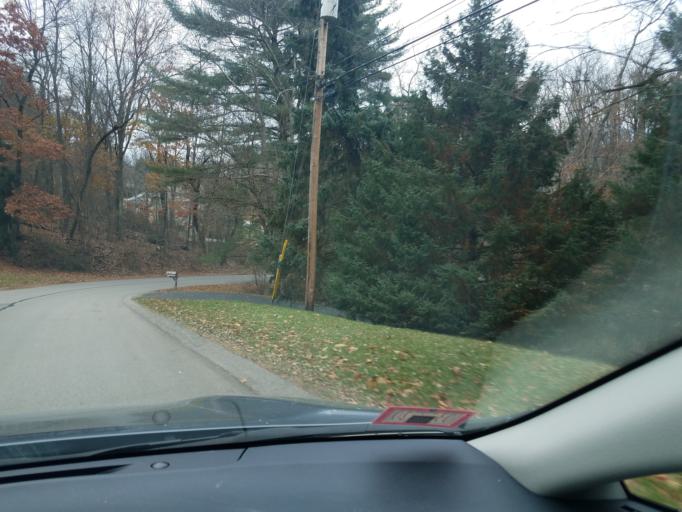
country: US
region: Pennsylvania
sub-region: Allegheny County
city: Franklin Park
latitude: 40.5665
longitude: -80.0678
